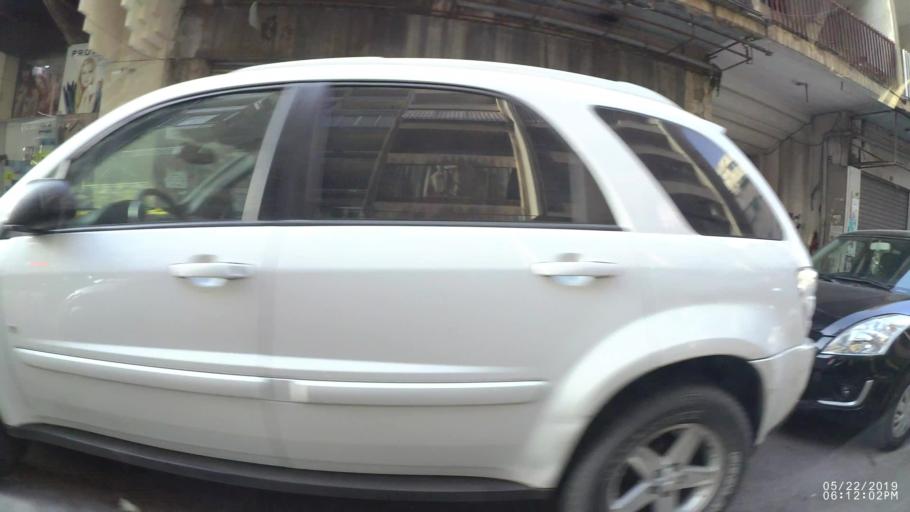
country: LB
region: Beyrouth
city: Ra's Bayrut
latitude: 33.8968
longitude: 35.4796
